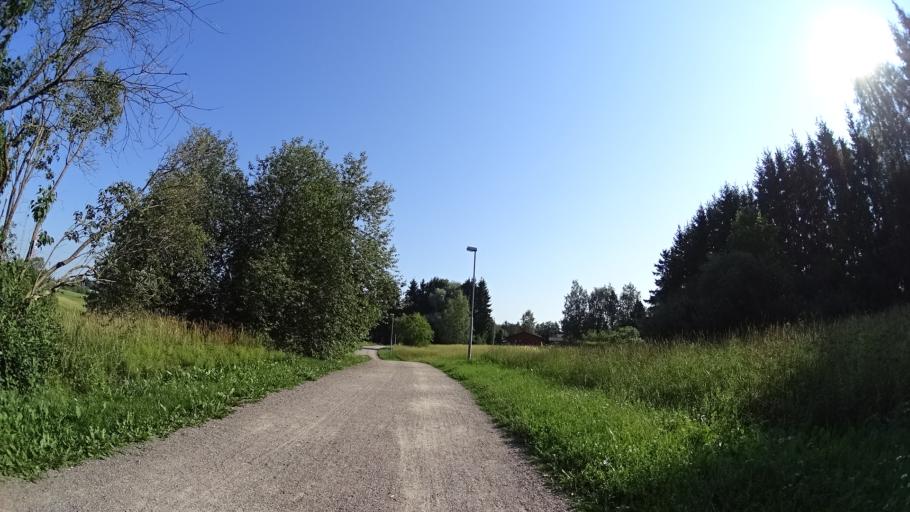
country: FI
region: Uusimaa
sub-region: Helsinki
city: Vantaa
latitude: 60.2831
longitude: 24.9984
